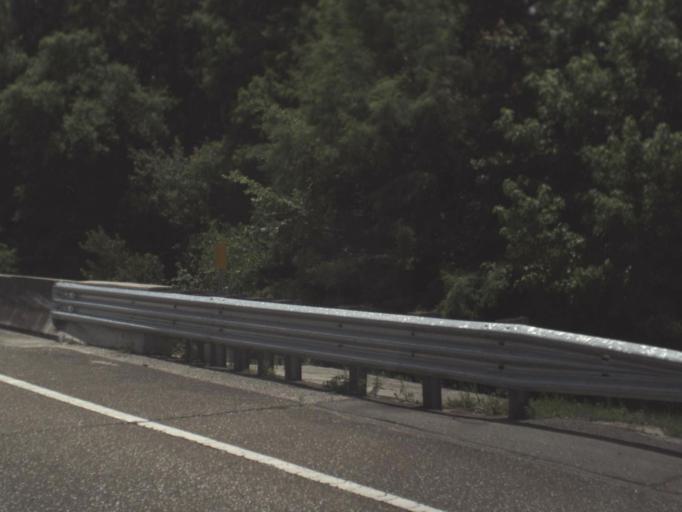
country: US
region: Florida
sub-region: Duval County
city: Jacksonville
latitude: 30.4098
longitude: -81.7462
